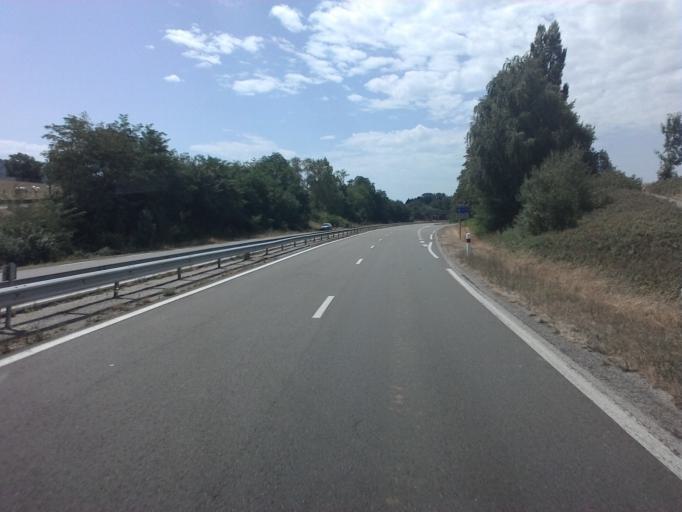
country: FR
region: Bourgogne
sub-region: Departement de Saone-et-Loire
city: Cuiseaux
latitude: 46.5048
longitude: 5.3866
